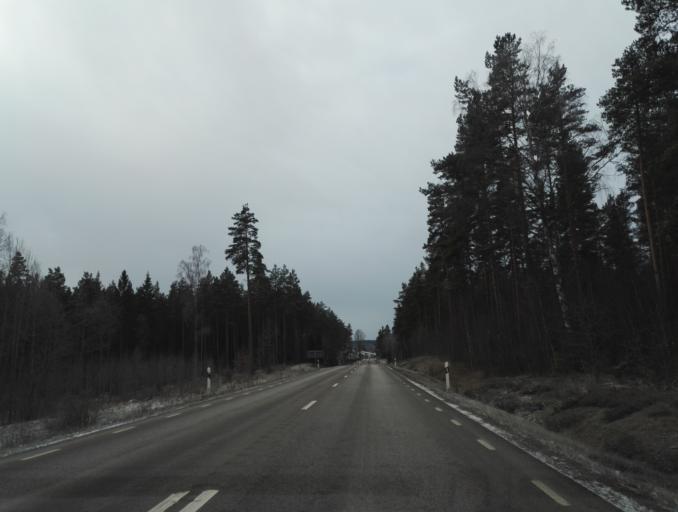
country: SE
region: Kalmar
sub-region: Hultsfreds Kommun
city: Virserum
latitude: 57.4192
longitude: 15.6285
